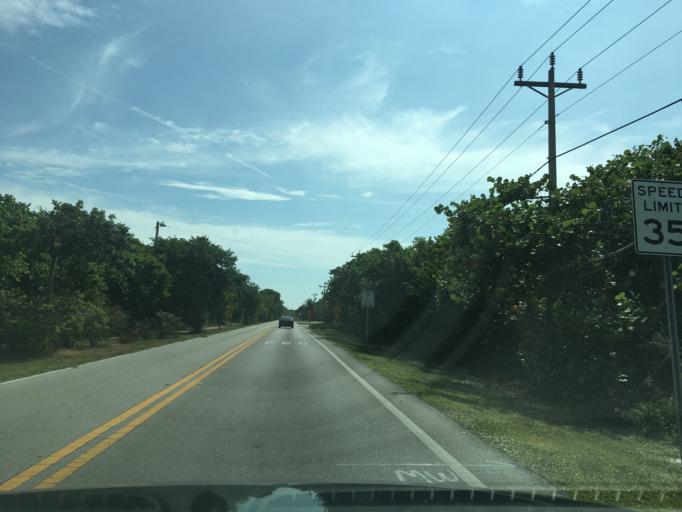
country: US
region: Florida
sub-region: Lee County
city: Saint James City
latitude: 26.4668
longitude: -82.1533
